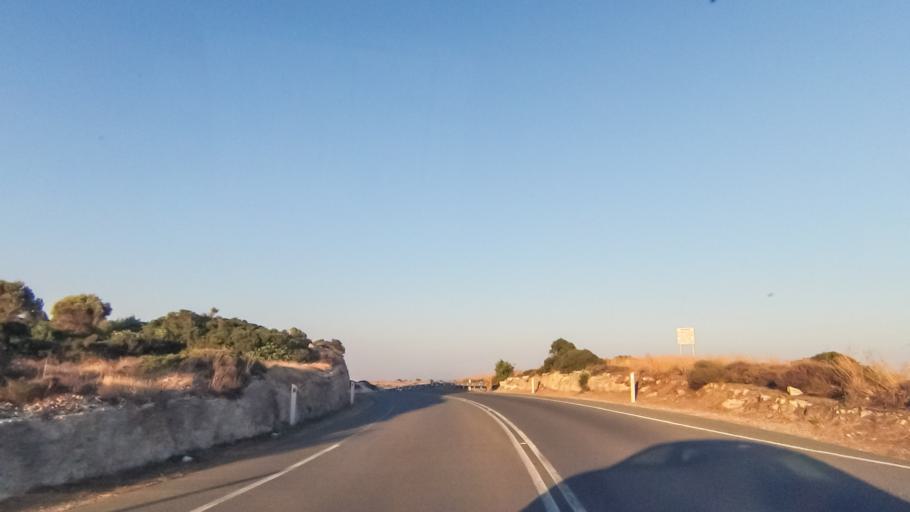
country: CY
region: Limassol
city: Erimi
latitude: 34.6696
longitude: 32.8777
